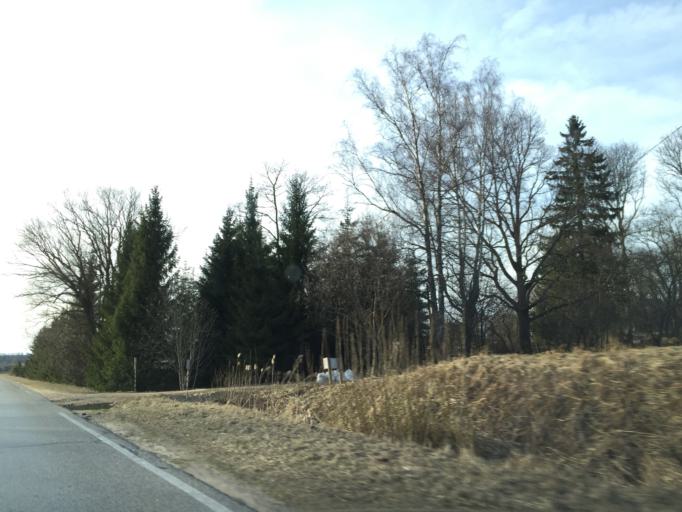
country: LV
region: Krimulda
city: Ragana
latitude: 57.1642
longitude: 24.7832
